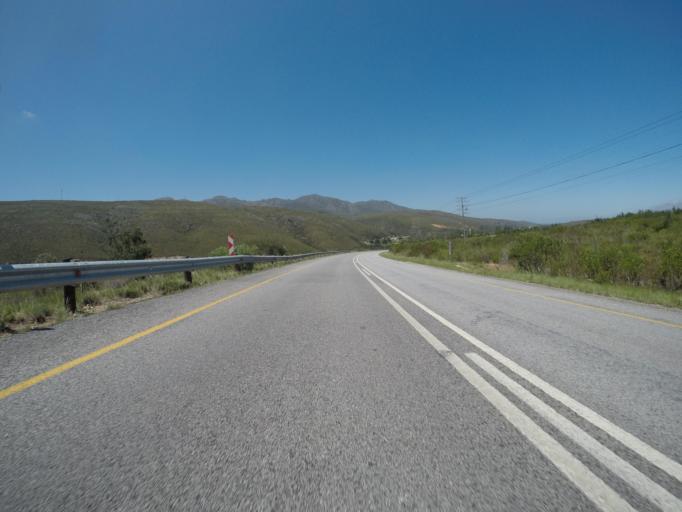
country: ZA
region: Eastern Cape
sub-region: Cacadu District Municipality
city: Kareedouw
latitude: -33.9426
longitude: 24.3080
